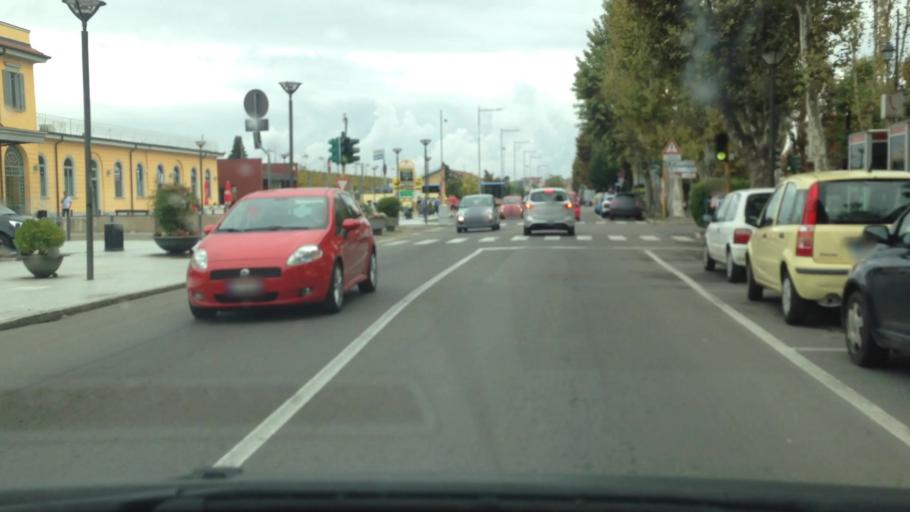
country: IT
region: Piedmont
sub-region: Provincia di Alessandria
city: Tortona
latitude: 44.8995
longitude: 8.8619
